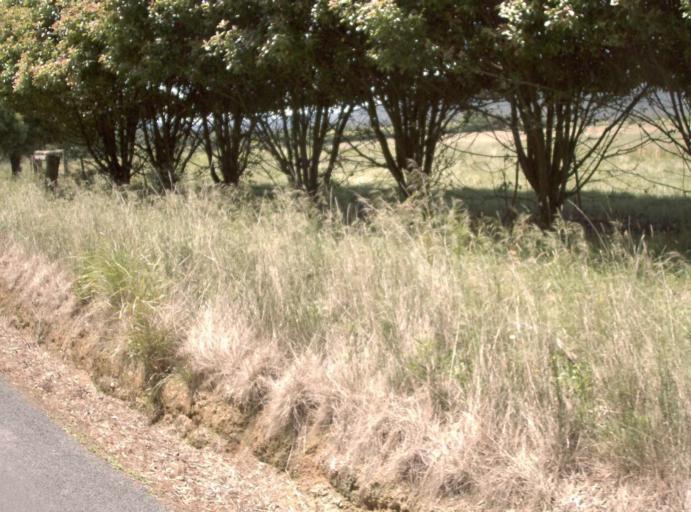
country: AU
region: New South Wales
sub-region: Bombala
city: Bombala
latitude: -37.4209
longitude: 149.0090
